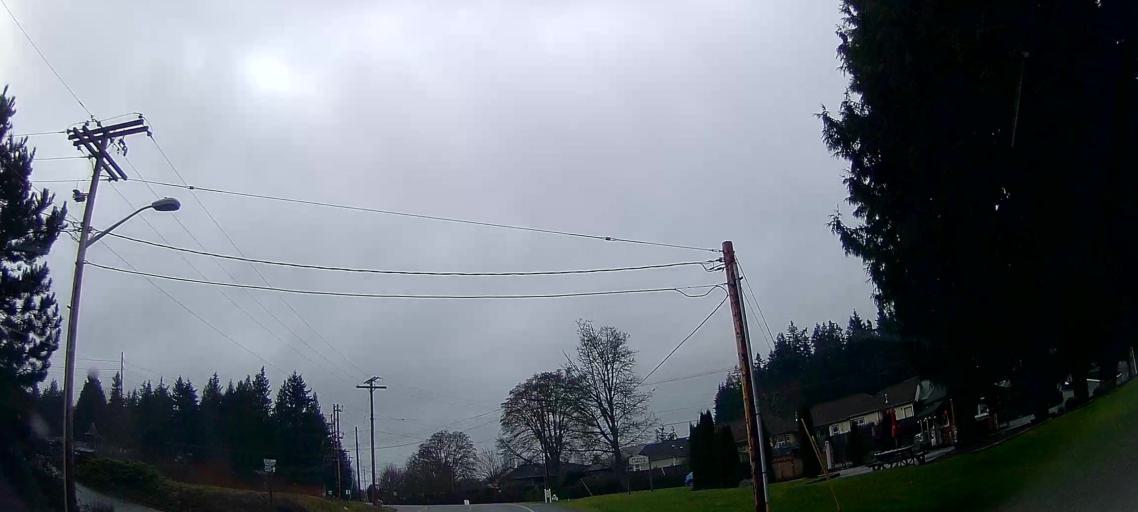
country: US
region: Washington
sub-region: Island County
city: Freeland
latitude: 48.0100
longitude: -122.5178
